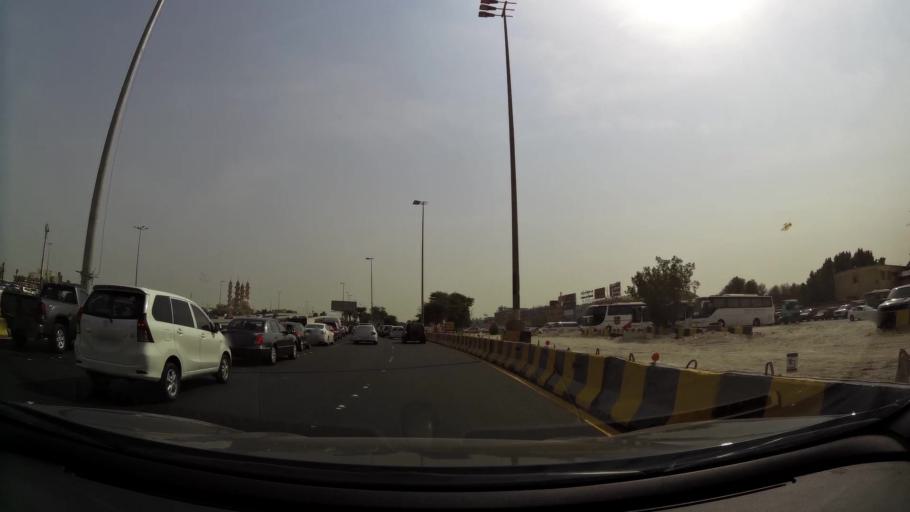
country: KW
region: Al Asimah
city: Ash Shamiyah
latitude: 29.3355
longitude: 47.9499
